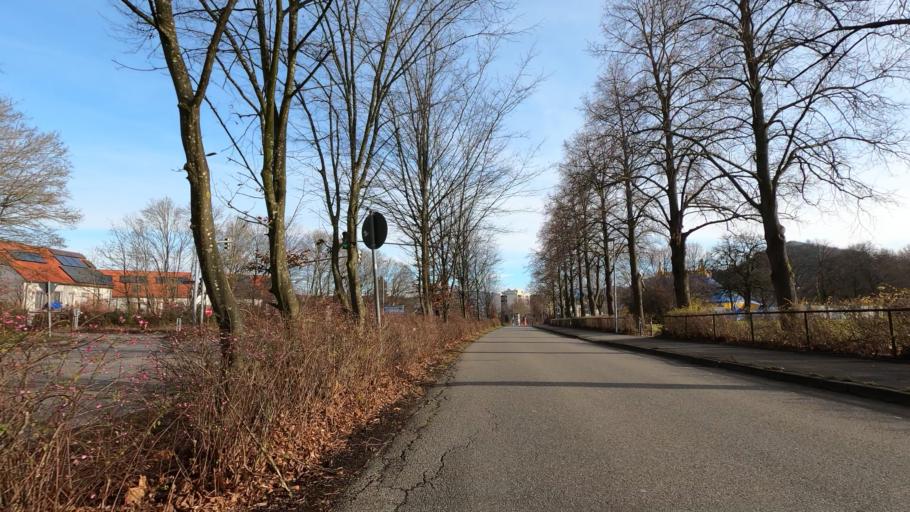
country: DE
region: Baden-Wuerttemberg
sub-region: Tuebingen Region
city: Reutlingen
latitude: 48.4803
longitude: 9.1930
